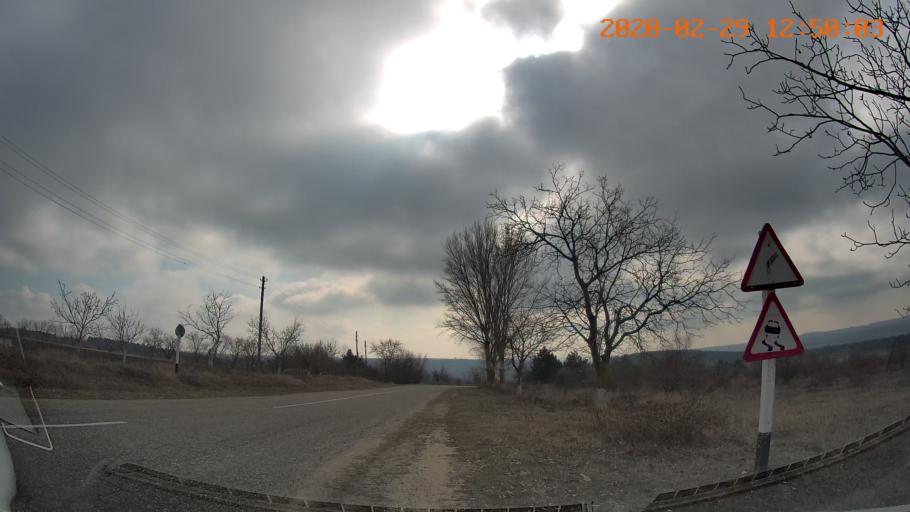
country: MD
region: Telenesti
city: Camenca
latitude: 48.1263
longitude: 28.7412
